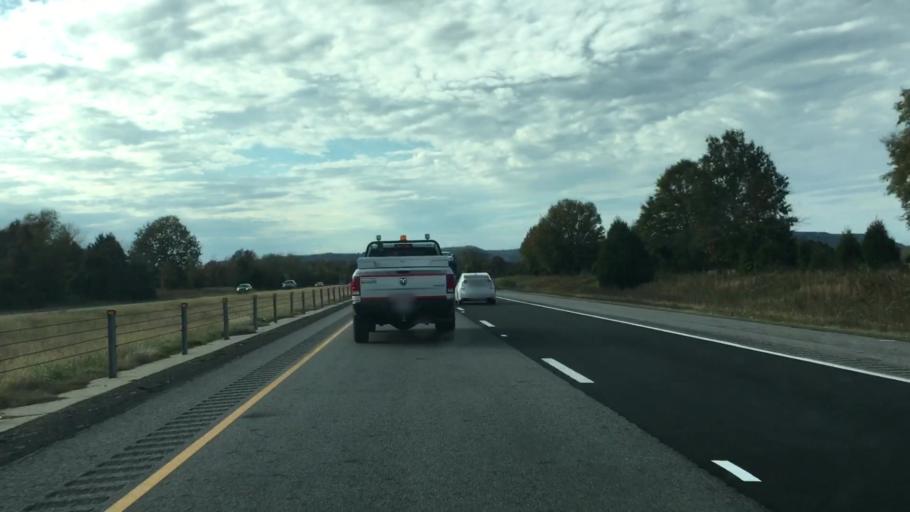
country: US
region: Arkansas
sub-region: Pope County
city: Atkins
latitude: 35.2489
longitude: -92.8785
